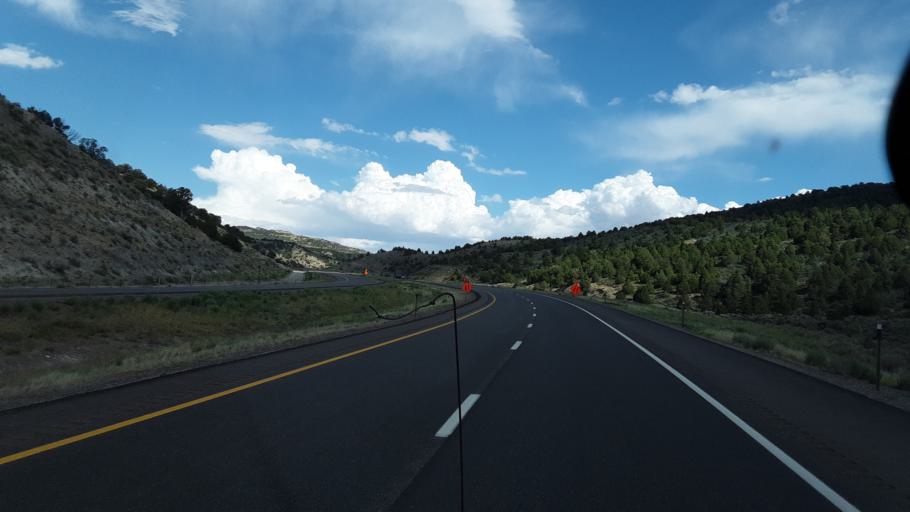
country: US
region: Utah
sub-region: Sevier County
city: Salina
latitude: 38.8071
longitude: -111.5294
